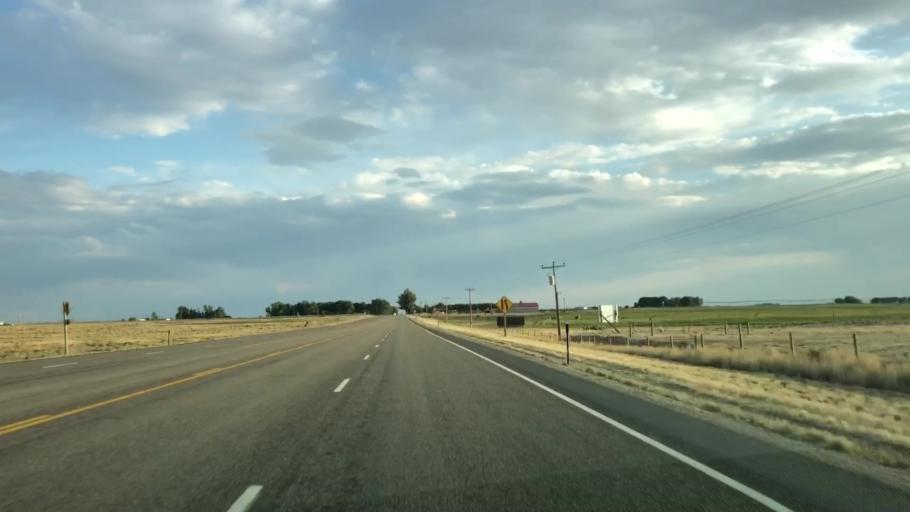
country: US
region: Wyoming
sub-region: Sweetwater County
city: North Rock Springs
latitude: 42.0644
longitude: -109.4382
